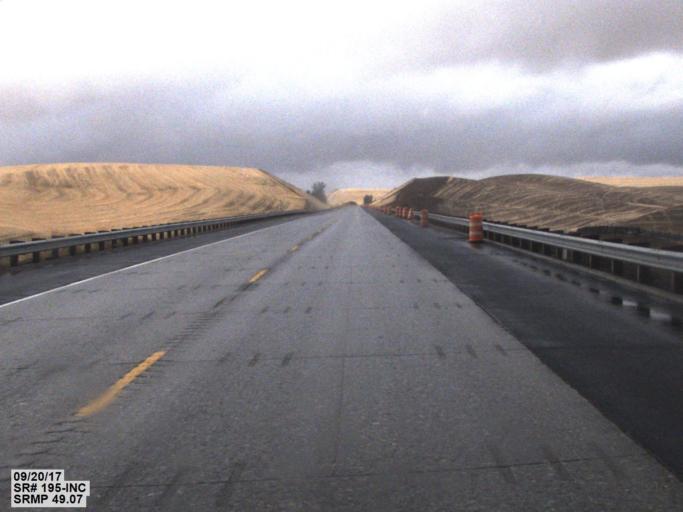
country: US
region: Washington
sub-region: Whitman County
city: Colfax
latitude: 47.0212
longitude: -117.3581
